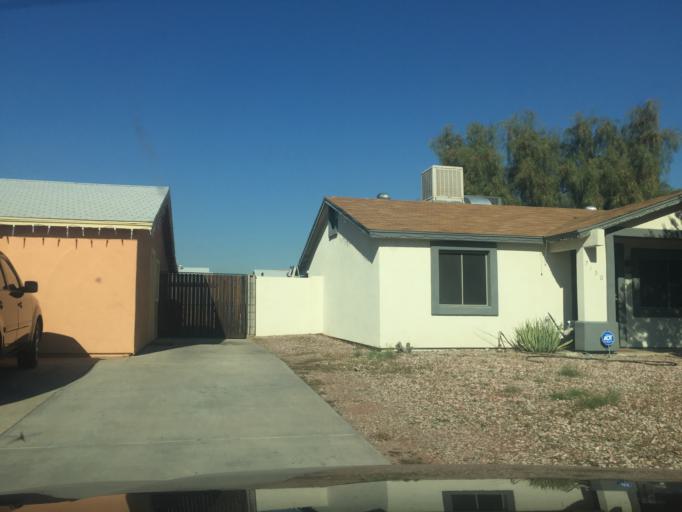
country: US
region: Arizona
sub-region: Maricopa County
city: Tolleson
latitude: 33.4706
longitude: -112.2144
